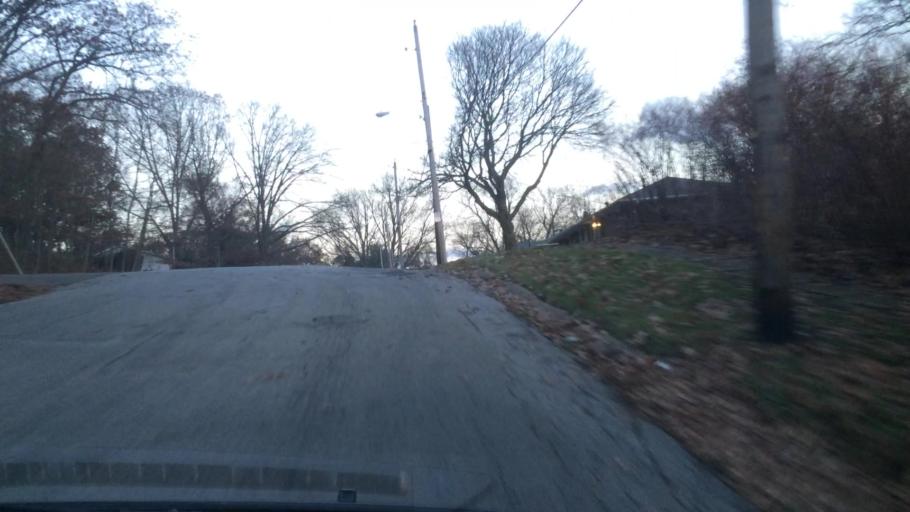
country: US
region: Ohio
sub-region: Summit County
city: Sawyerwood
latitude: 41.0652
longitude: -81.4571
